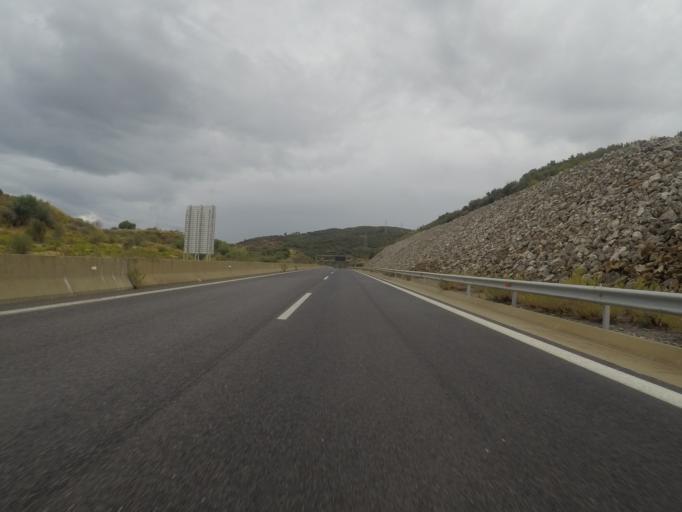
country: GR
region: Peloponnese
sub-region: Nomos Messinias
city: Meligalas
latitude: 37.2616
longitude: 22.0255
